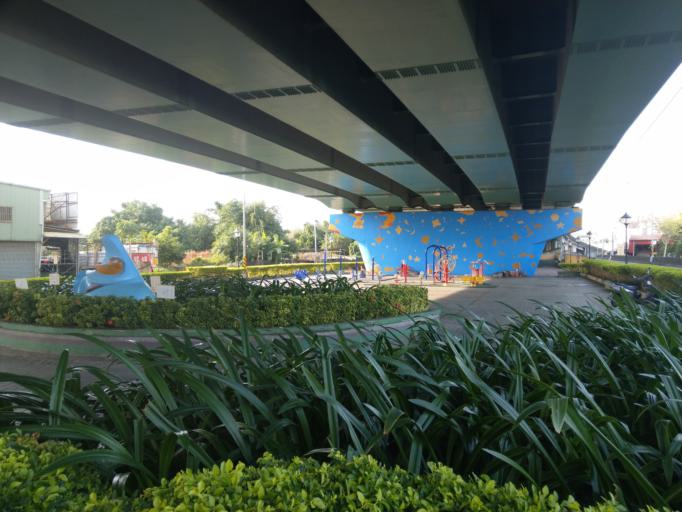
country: TW
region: Taiwan
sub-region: Taichung City
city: Taichung
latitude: 24.1080
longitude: 120.6717
